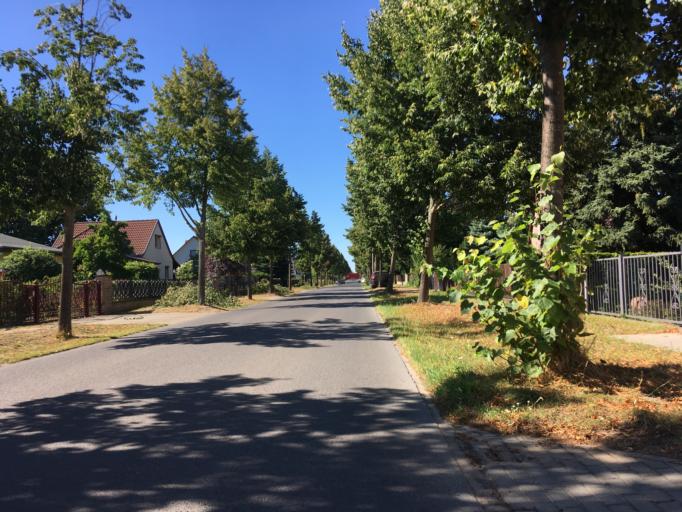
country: DE
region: Brandenburg
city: Schulzendorf
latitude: 52.3577
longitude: 13.5872
